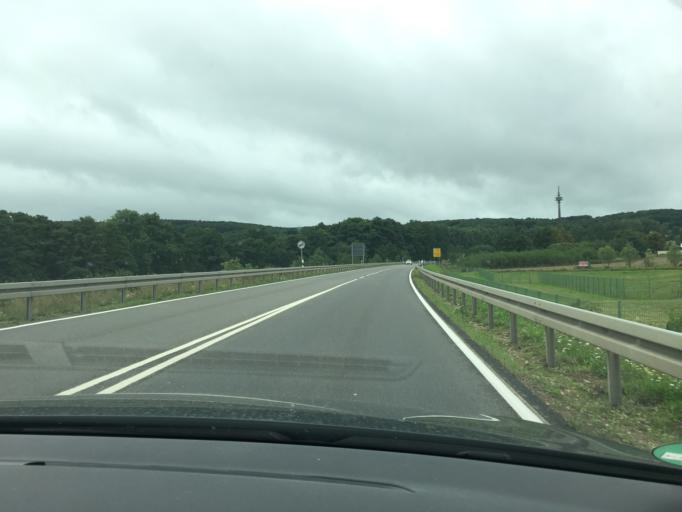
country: DE
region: North Rhine-Westphalia
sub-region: Regierungsbezirk Koln
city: Kreuzau
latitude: 50.7483
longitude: 6.4274
